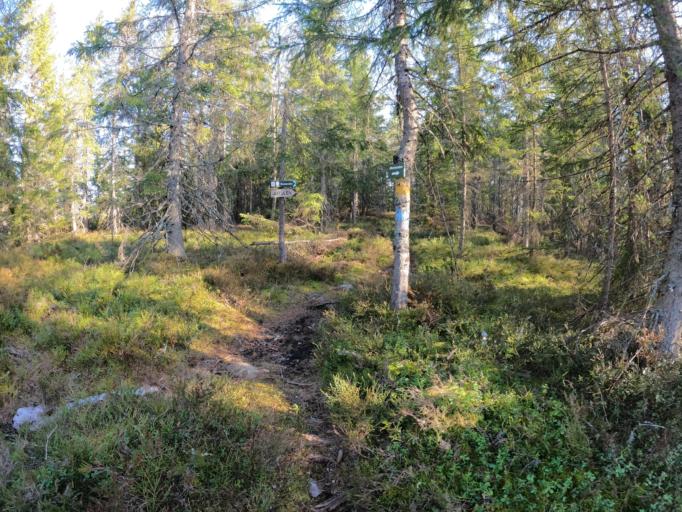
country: NO
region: Akershus
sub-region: Nannestad
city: Teigebyen
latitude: 60.2384
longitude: 10.9600
